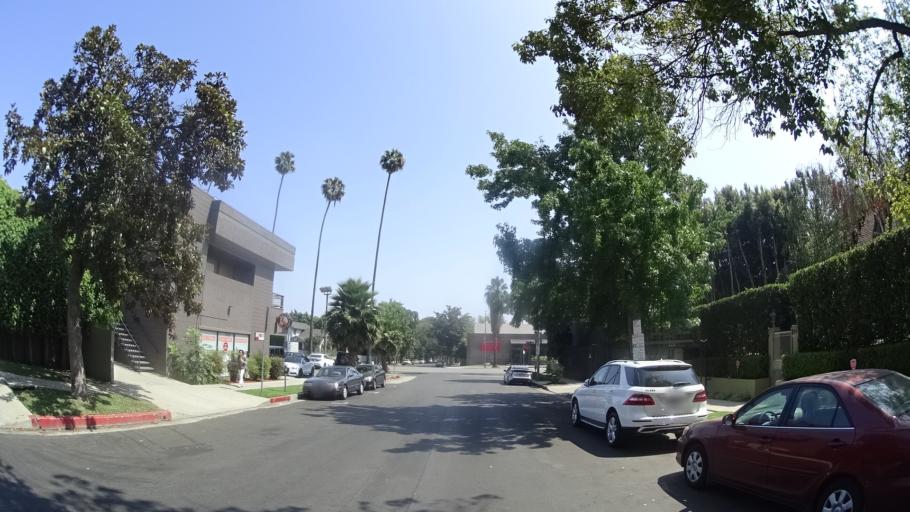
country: US
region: California
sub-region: Los Angeles County
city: West Hollywood
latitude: 34.0987
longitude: -118.3594
